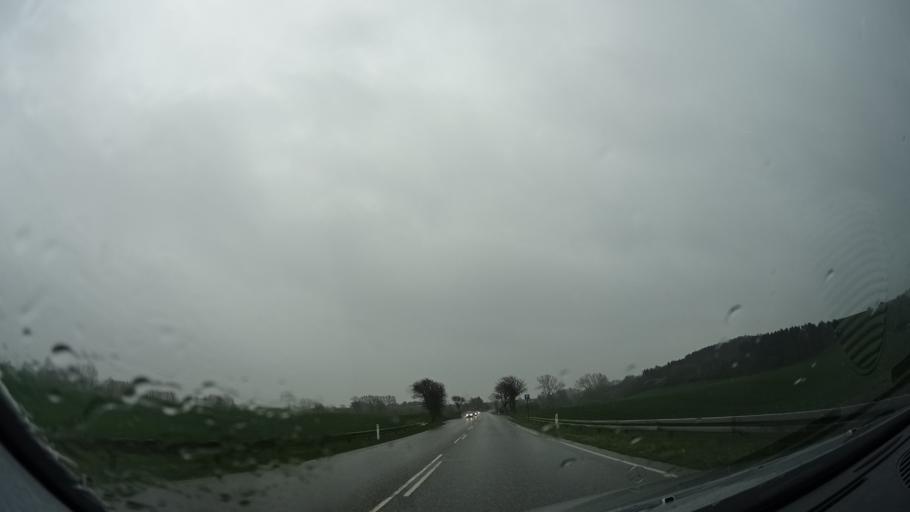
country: DK
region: Zealand
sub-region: Odsherred Kommune
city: Asnaes
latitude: 55.8194
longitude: 11.5789
